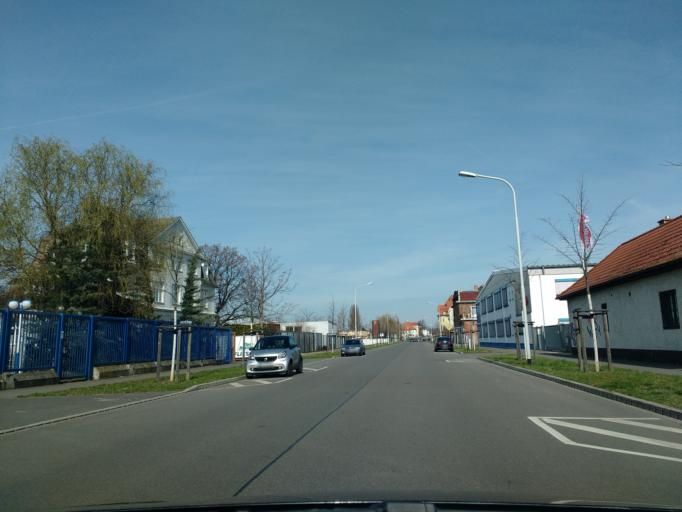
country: DE
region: Saxony-Anhalt
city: Halle (Saale)
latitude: 51.4816
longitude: 12.0120
